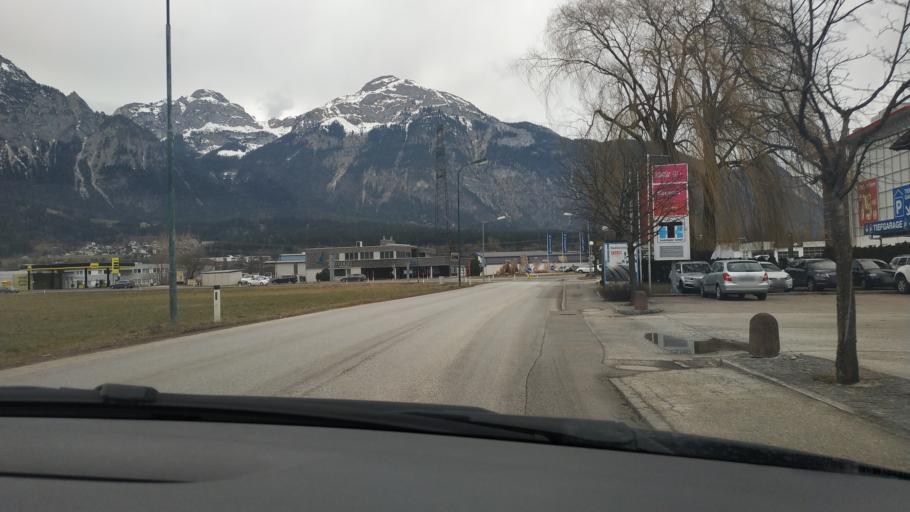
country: AT
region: Tyrol
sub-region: Politischer Bezirk Schwaz
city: Strass im Zillertal
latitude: 47.3967
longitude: 11.8177
